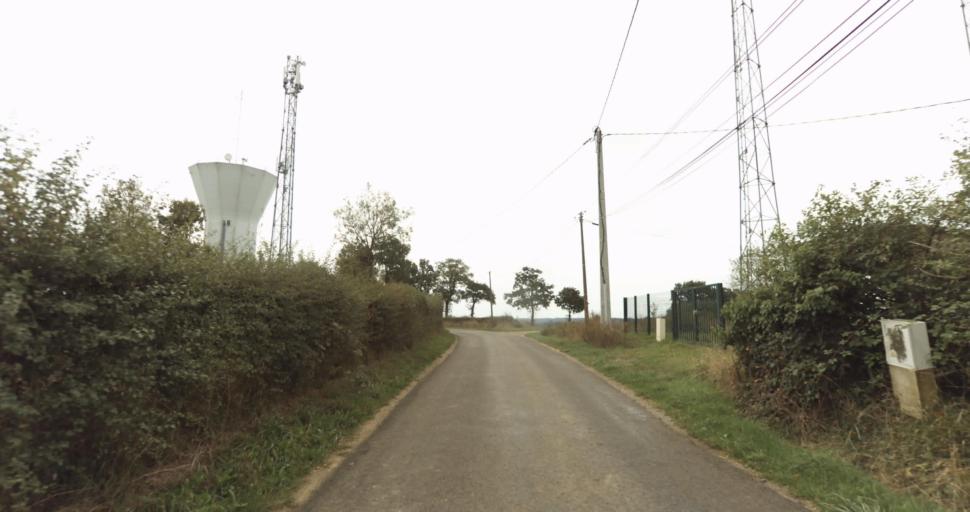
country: FR
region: Lower Normandy
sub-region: Departement de l'Orne
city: Gace
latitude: 48.7165
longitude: 0.3206
